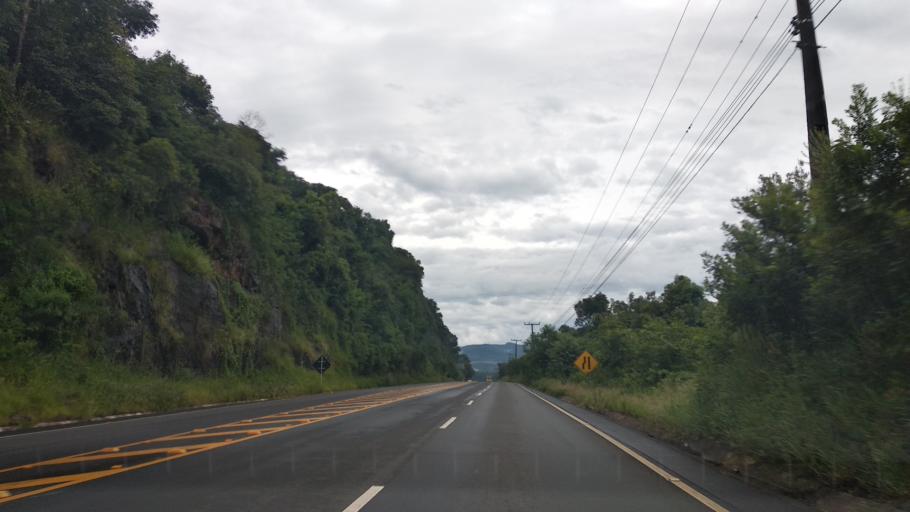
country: BR
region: Santa Catarina
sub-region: Videira
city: Videira
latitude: -27.0637
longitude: -51.2299
